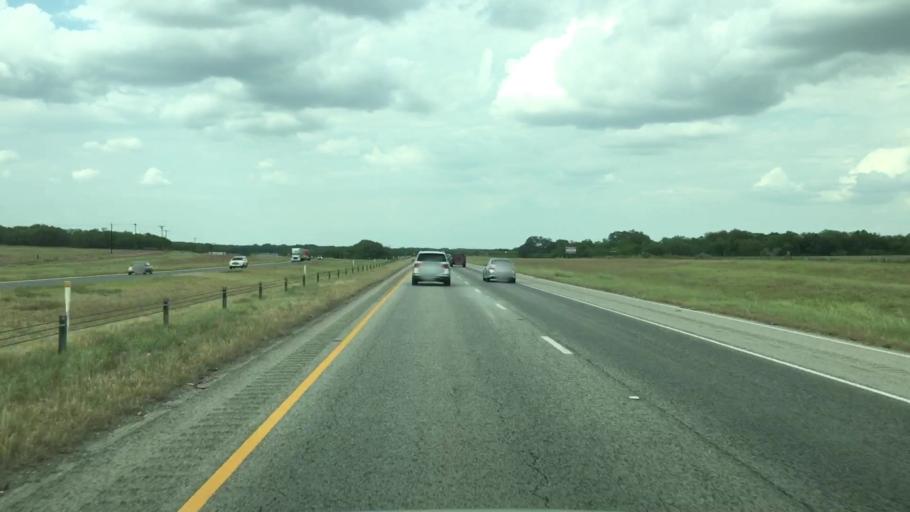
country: US
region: Texas
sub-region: Atascosa County
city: Pleasanton
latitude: 29.0188
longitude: -98.4310
